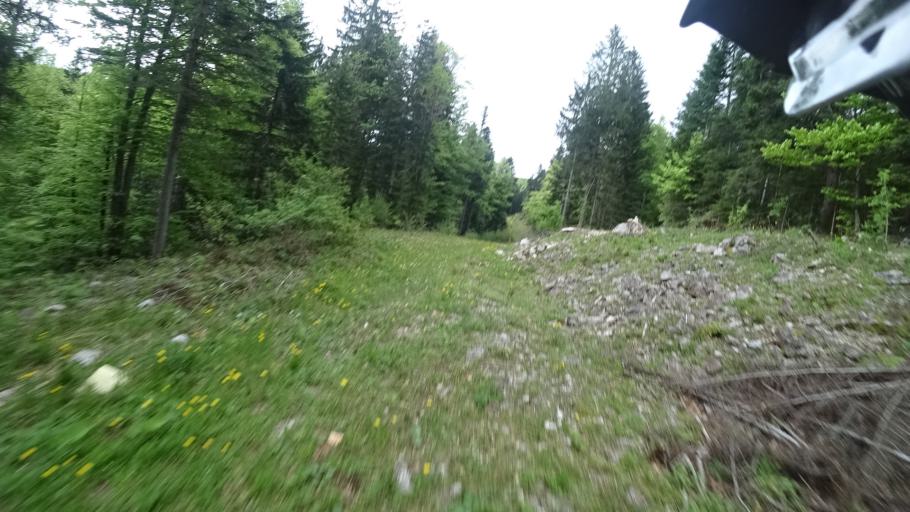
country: HR
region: Karlovacka
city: Plaski
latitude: 44.9587
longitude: 15.4125
